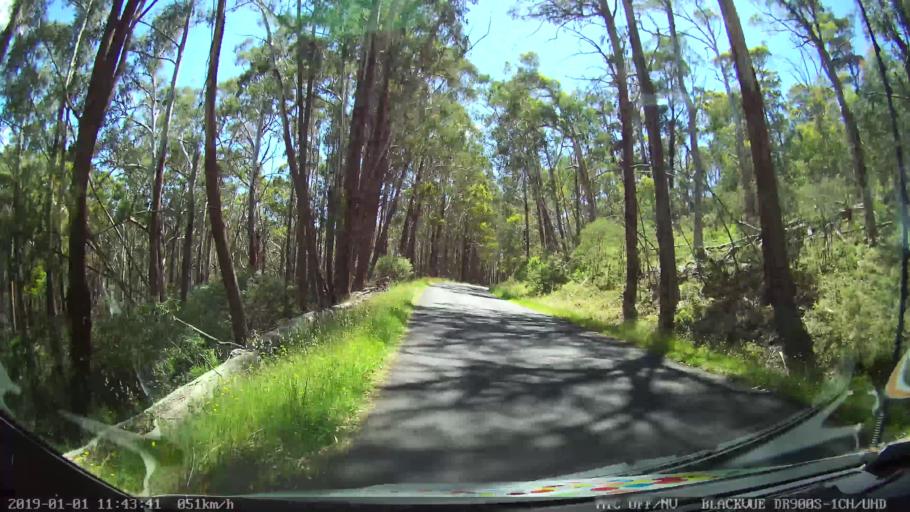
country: AU
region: New South Wales
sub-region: Snowy River
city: Jindabyne
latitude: -35.9043
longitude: 148.3878
